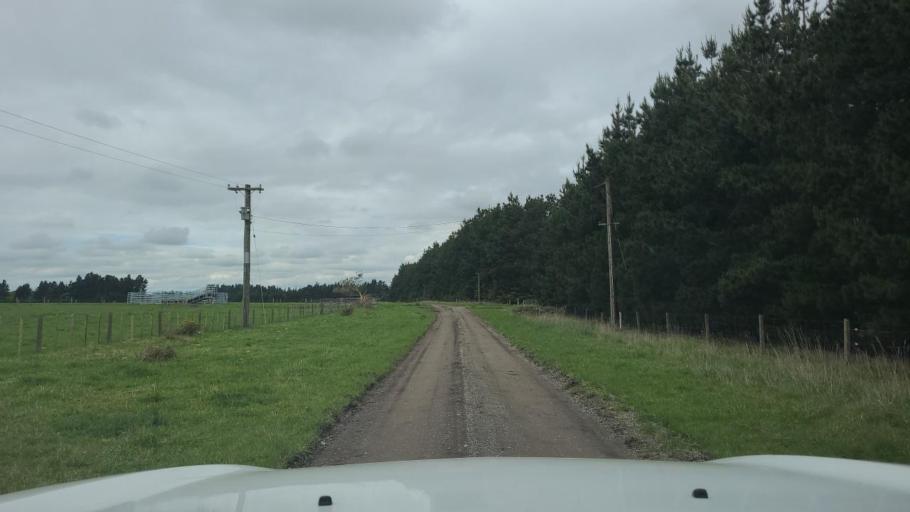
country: NZ
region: Wellington
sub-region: Upper Hutt City
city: Upper Hutt
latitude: -41.0910
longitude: 175.3513
